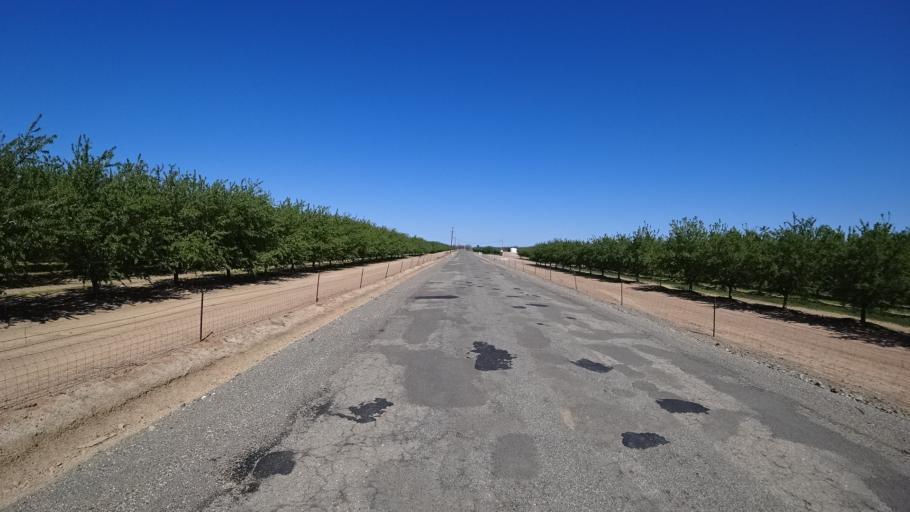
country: US
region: California
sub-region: Glenn County
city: Orland
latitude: 39.6565
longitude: -122.2346
